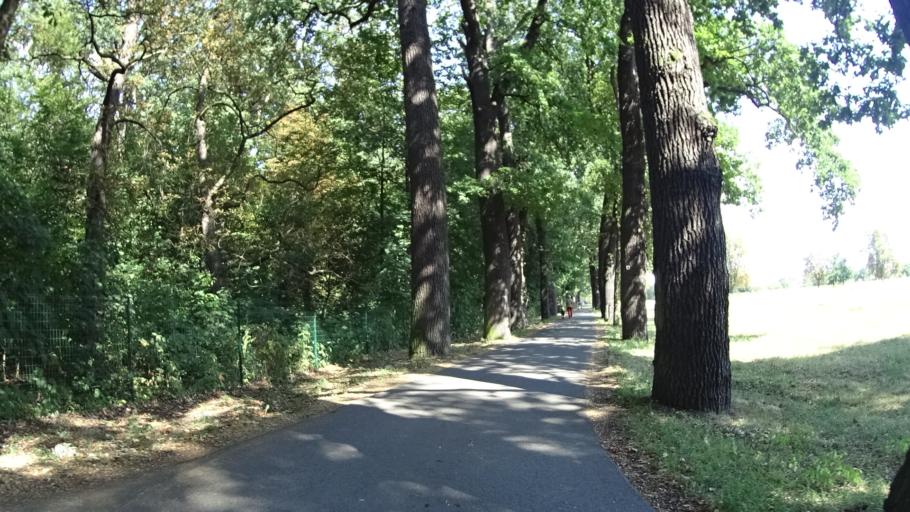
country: DE
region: Saxony
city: Zittau
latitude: 50.8985
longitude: 14.8360
